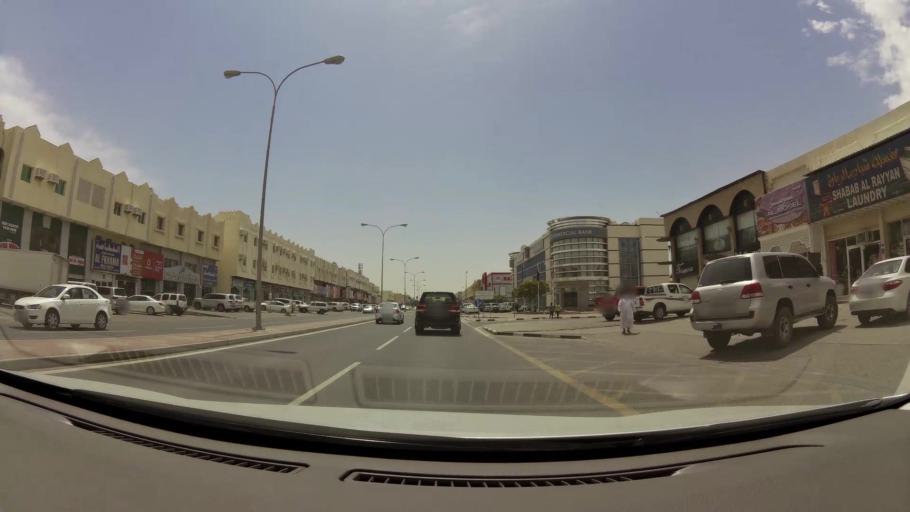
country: QA
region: Baladiyat ar Rayyan
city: Ar Rayyan
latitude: 25.2917
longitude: 51.4199
